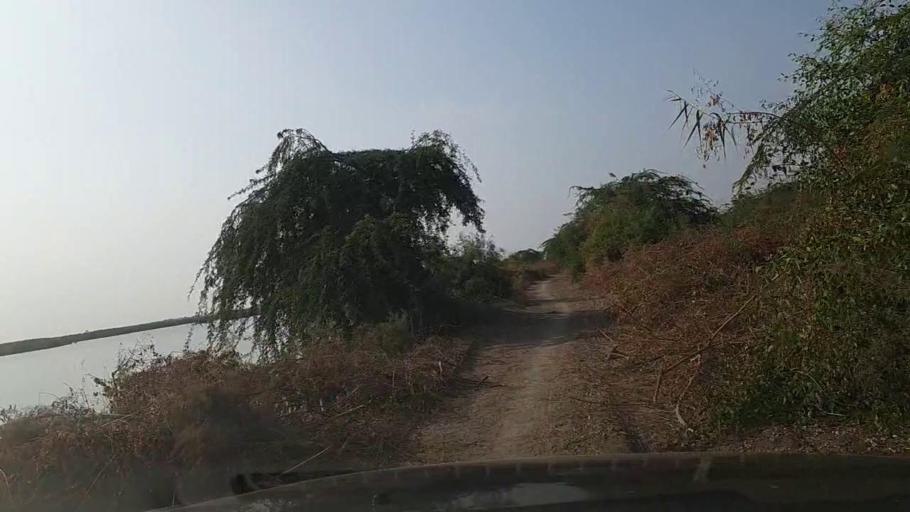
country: PK
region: Sindh
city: Mirpur Batoro
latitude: 24.6490
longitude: 68.2755
